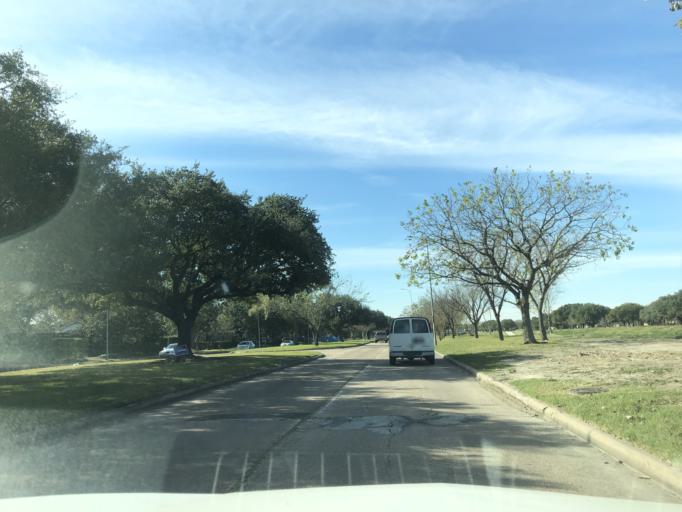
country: US
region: Texas
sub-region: Harris County
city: Bellaire
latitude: 29.6781
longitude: -95.4691
